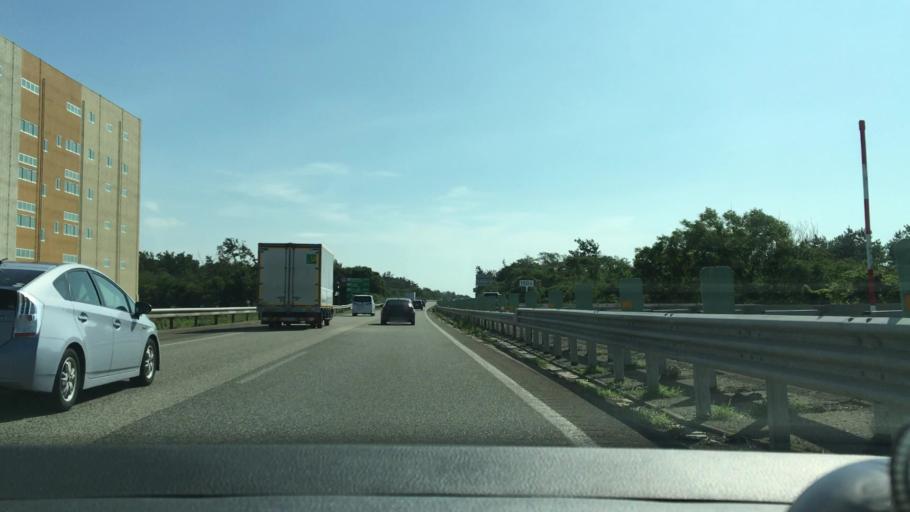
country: JP
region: Ishikawa
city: Matsuto
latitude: 36.5004
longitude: 136.4940
